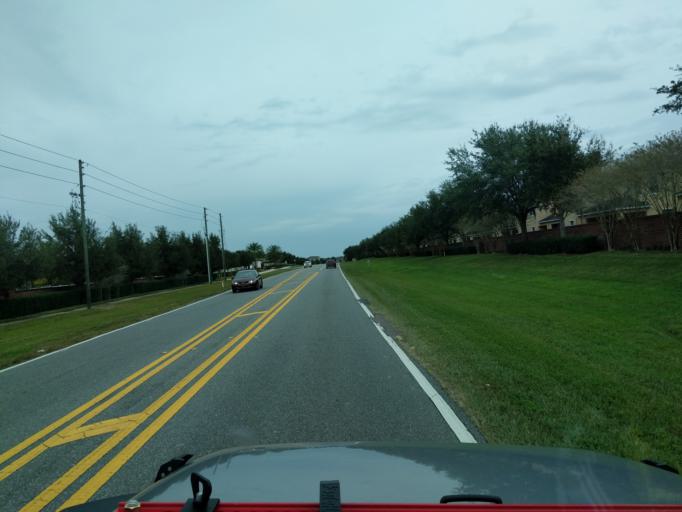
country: US
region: Florida
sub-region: Orange County
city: Oakland
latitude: 28.5208
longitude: -81.6202
